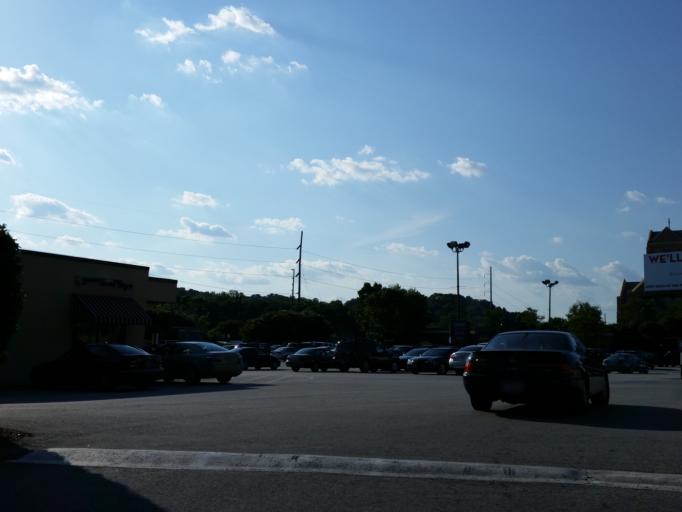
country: US
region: Georgia
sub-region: Cobb County
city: Vinings
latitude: 33.8503
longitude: -84.4293
